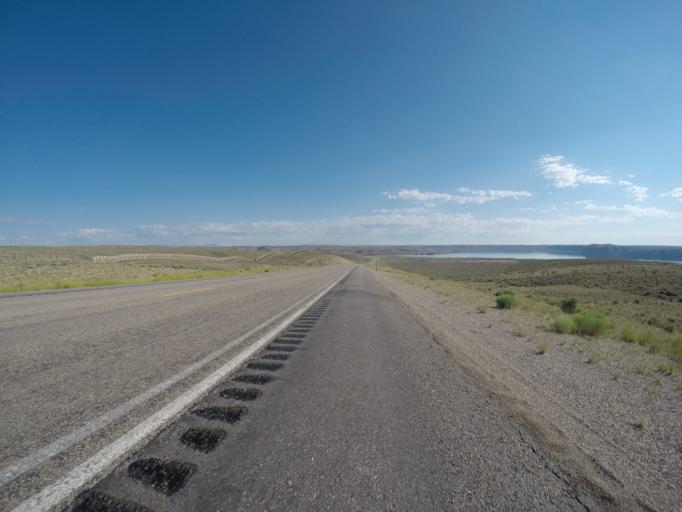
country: US
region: Wyoming
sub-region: Lincoln County
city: Kemmerer
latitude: 42.0635
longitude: -110.1625
